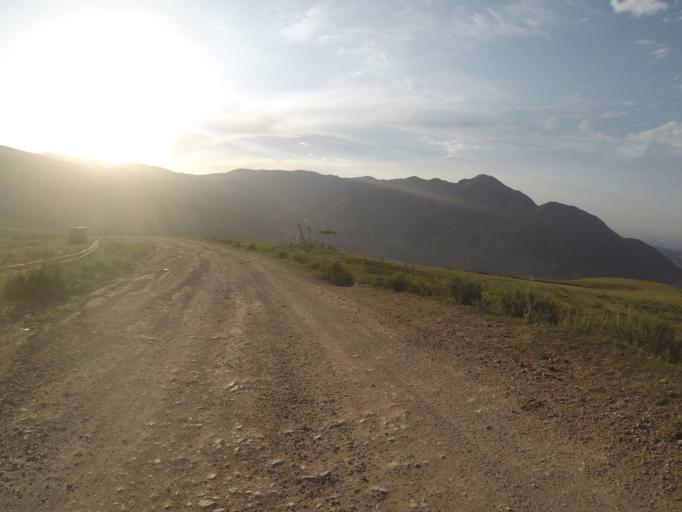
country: KG
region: Chuy
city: Bishkek
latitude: 42.6567
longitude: 74.6629
